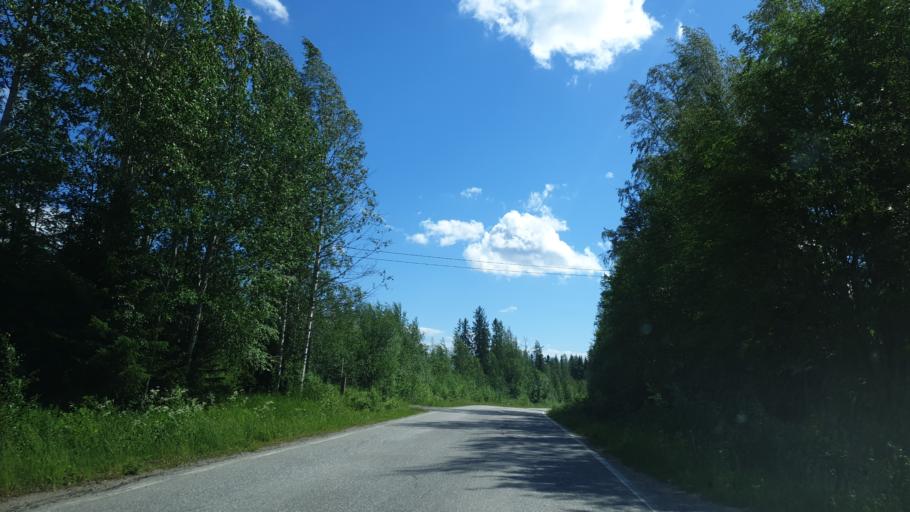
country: FI
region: Northern Savo
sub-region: Koillis-Savo
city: Kaavi
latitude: 62.9972
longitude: 28.5037
